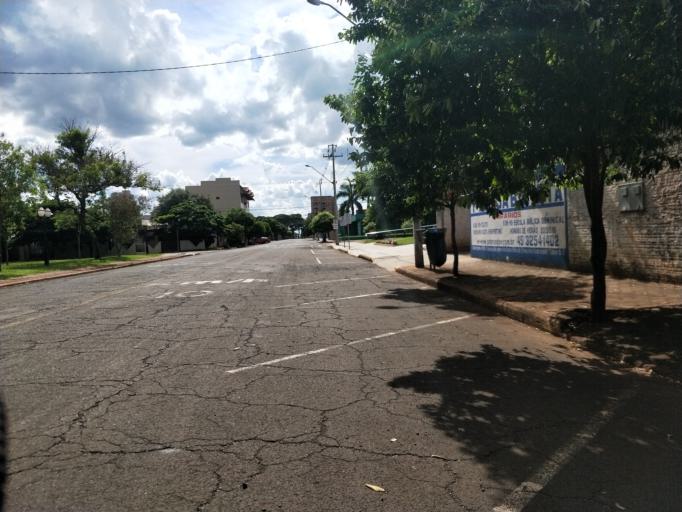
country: BR
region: Parana
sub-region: Marechal Candido Rondon
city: Marechal Candido Rondon
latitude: -24.5618
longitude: -54.0551
